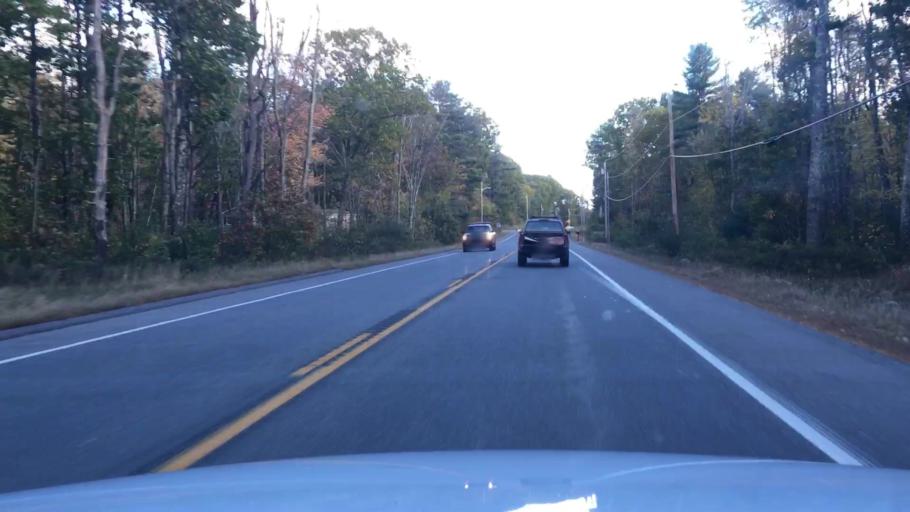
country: US
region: Maine
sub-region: York County
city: Wells Beach Station
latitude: 43.3414
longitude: -70.6389
